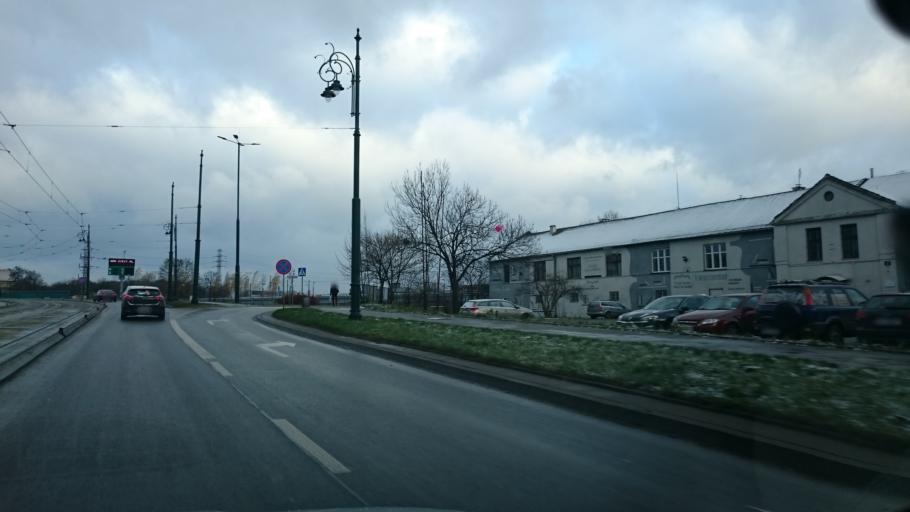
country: PL
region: Lesser Poland Voivodeship
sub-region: Krakow
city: Krakow
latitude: 50.0475
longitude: 19.9549
